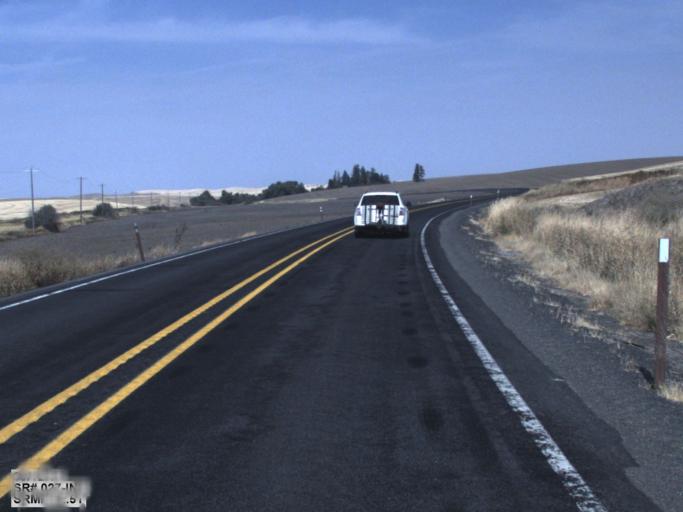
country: US
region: Washington
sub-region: Whitman County
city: Colfax
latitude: 47.1064
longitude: -117.1842
